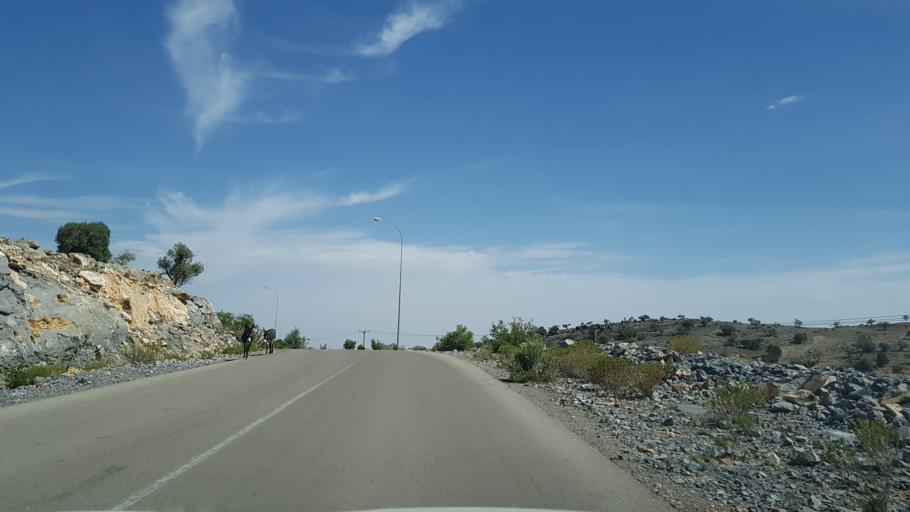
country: OM
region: Al Batinah
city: Bayt al `Awabi
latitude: 23.1255
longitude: 57.5998
